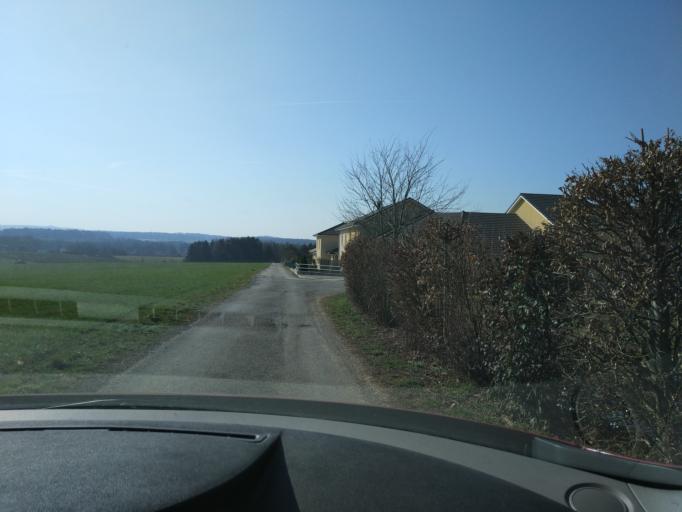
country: FR
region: Franche-Comte
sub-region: Departement du Doubs
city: Saone
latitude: 47.2167
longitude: 6.1160
